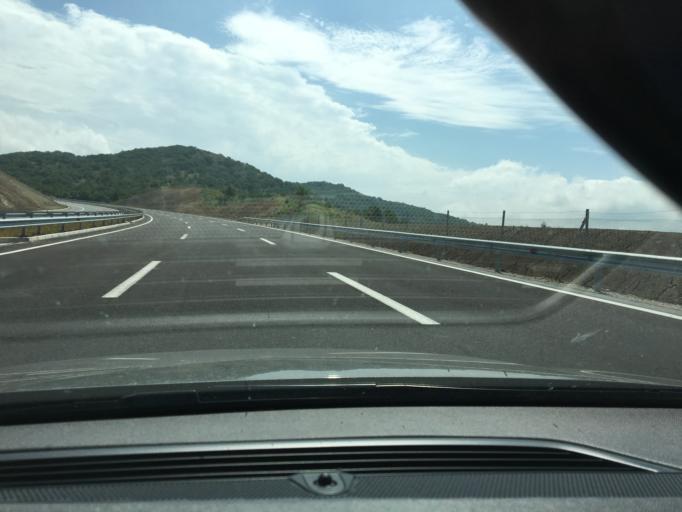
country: MK
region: Petrovec
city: Sredno Konjare
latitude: 41.9443
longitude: 21.7858
